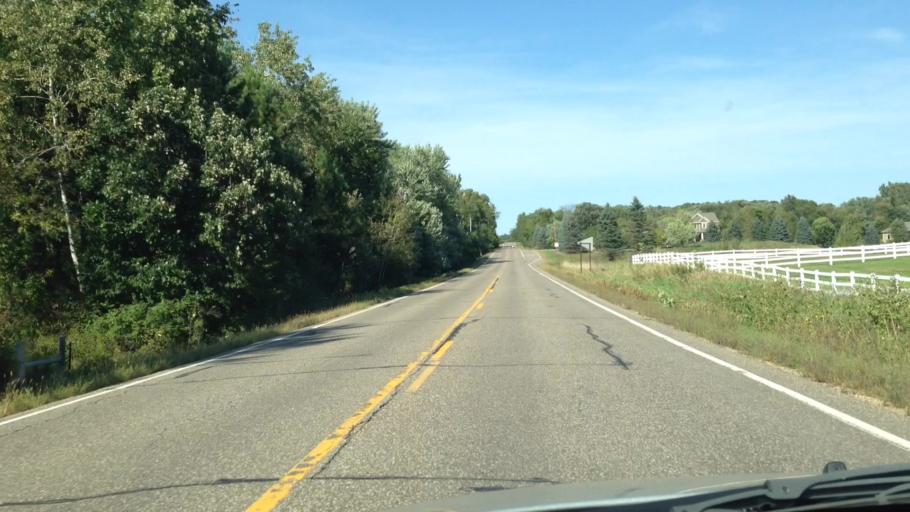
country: US
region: Minnesota
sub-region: Washington County
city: Stillwater
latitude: 45.1049
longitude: -92.8128
